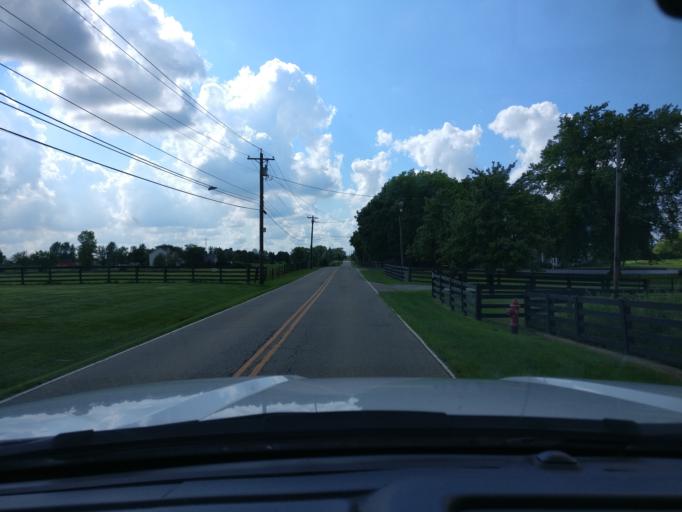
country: US
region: Ohio
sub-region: Warren County
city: Springboro
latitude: 39.5039
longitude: -84.2090
